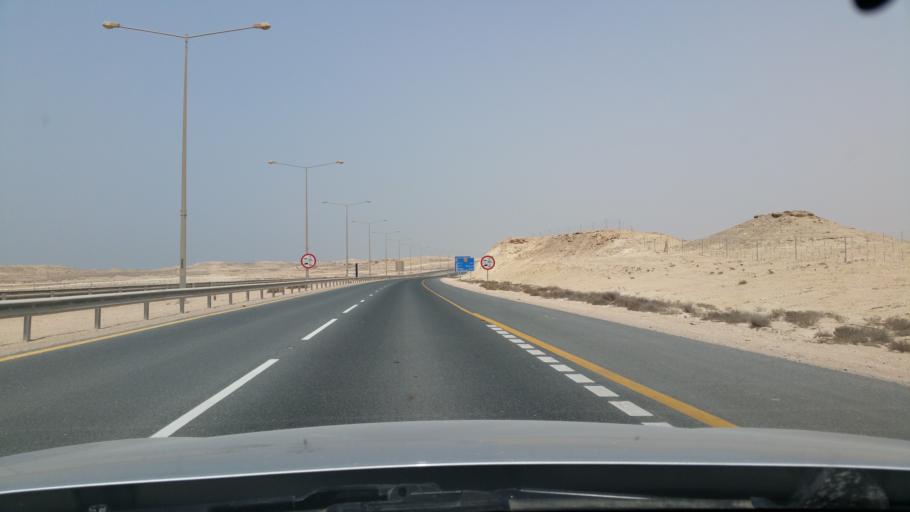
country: QA
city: Umm Bab
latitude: 25.2635
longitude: 50.7945
